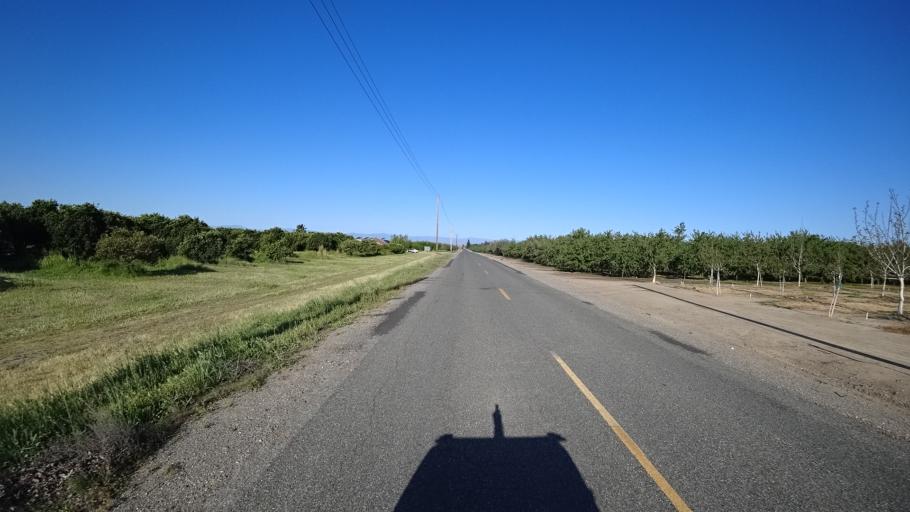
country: US
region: California
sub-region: Glenn County
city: Orland
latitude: 39.7108
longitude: -122.1620
